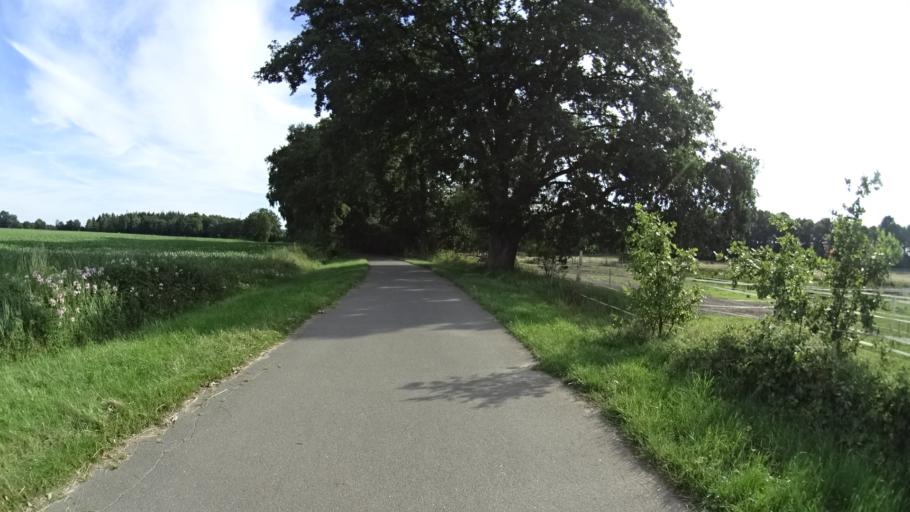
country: DE
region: Lower Saxony
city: Reppenstedt
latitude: 53.2409
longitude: 10.3588
